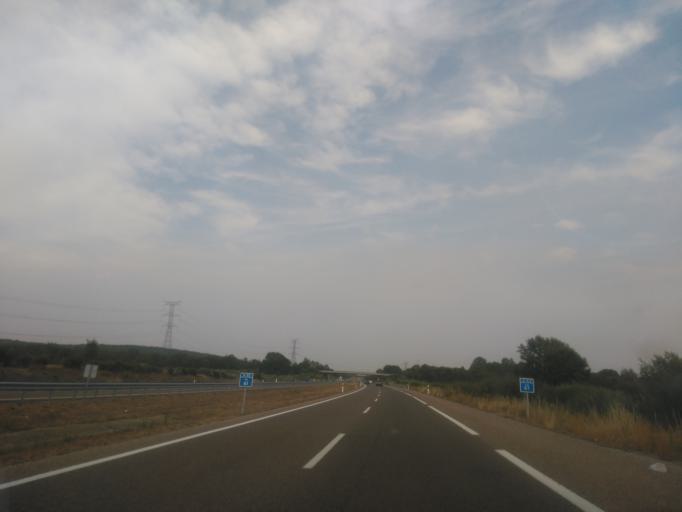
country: ES
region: Castille and Leon
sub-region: Provincia de Zamora
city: Cernadilla
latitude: 42.0227
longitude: -6.3929
